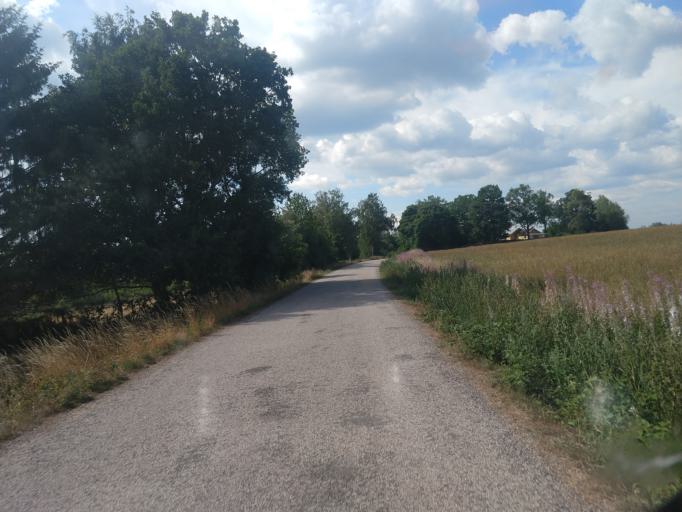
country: SE
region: Blekinge
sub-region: Karlskrona Kommun
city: Nattraby
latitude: 56.2465
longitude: 15.5393
